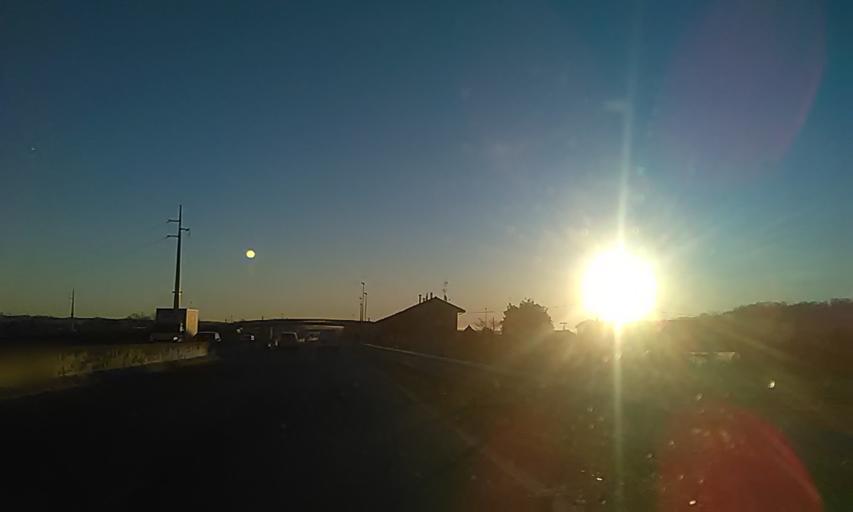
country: IT
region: Piedmont
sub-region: Provincia di Biella
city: Valdengo
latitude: 45.5547
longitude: 8.1364
